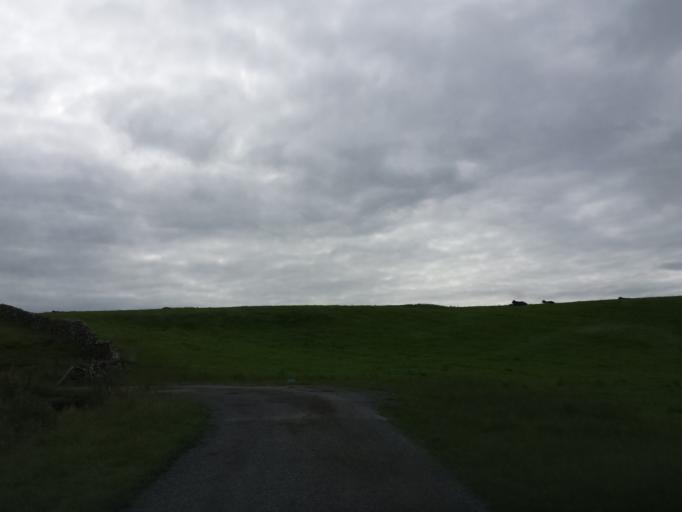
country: GB
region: Scotland
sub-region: Dumfries and Galloway
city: Stranraer
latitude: 54.8655
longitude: -5.1409
